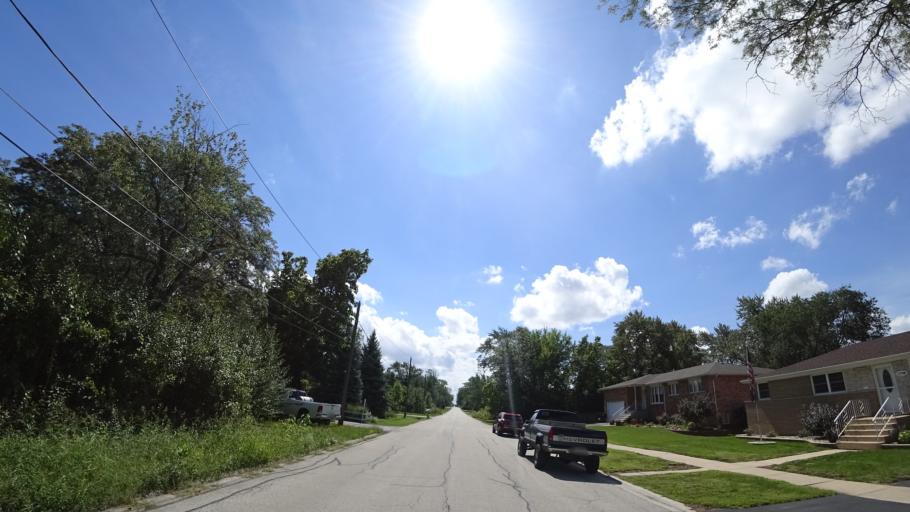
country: US
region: Illinois
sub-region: Cook County
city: Tinley Park
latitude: 41.5687
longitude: -87.7886
